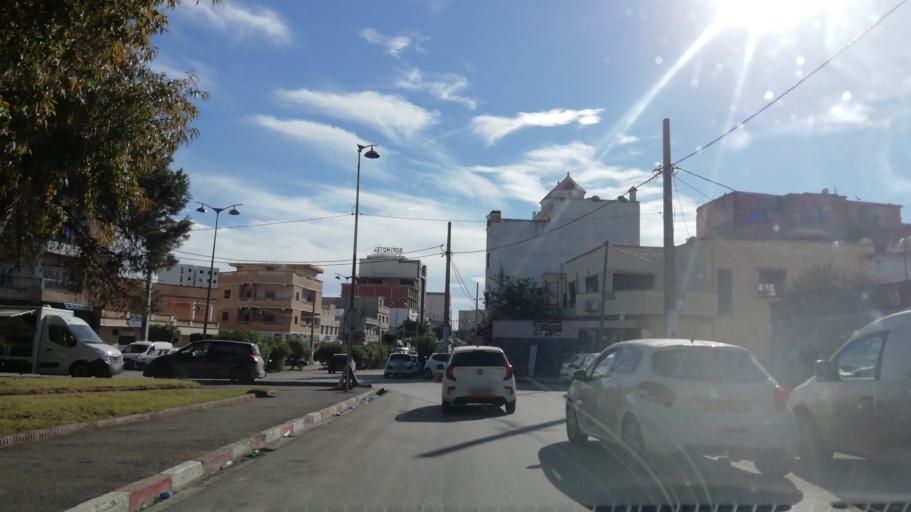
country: DZ
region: Oran
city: Oran
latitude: 35.6949
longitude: -0.6198
